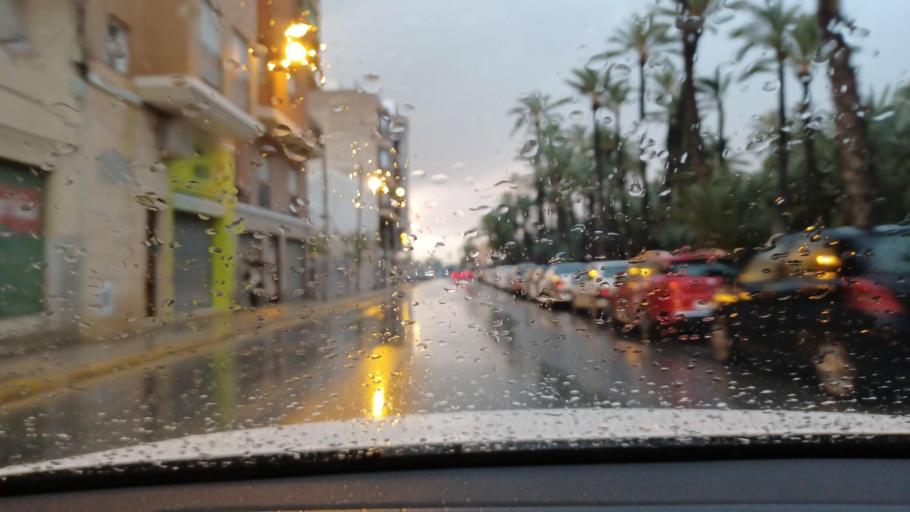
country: ES
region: Valencia
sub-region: Provincia de Alicante
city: Elche
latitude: 38.2560
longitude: -0.6973
